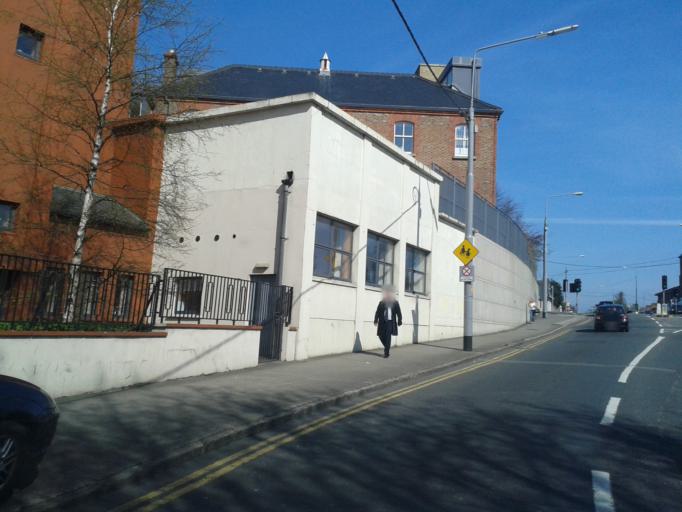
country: IE
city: Milltown
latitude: 53.3124
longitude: -6.2476
